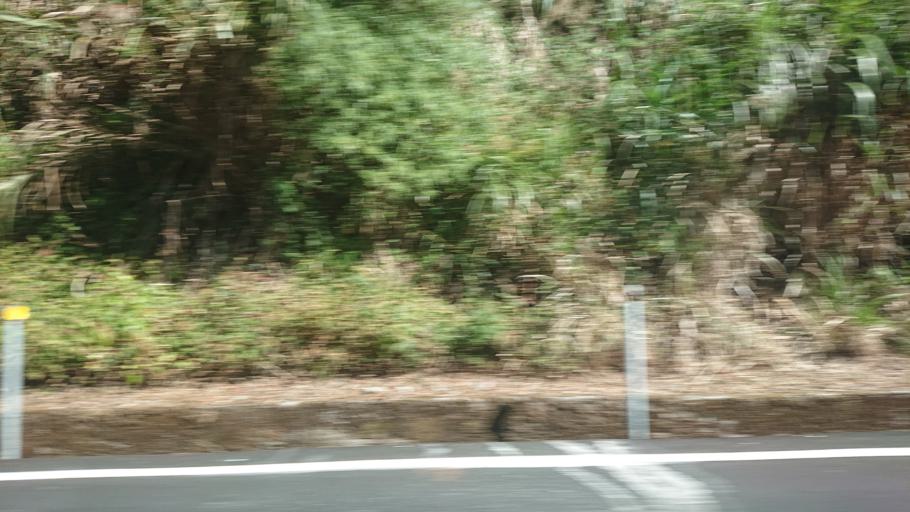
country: TW
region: Taiwan
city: Lugu
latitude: 23.4880
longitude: 120.8218
